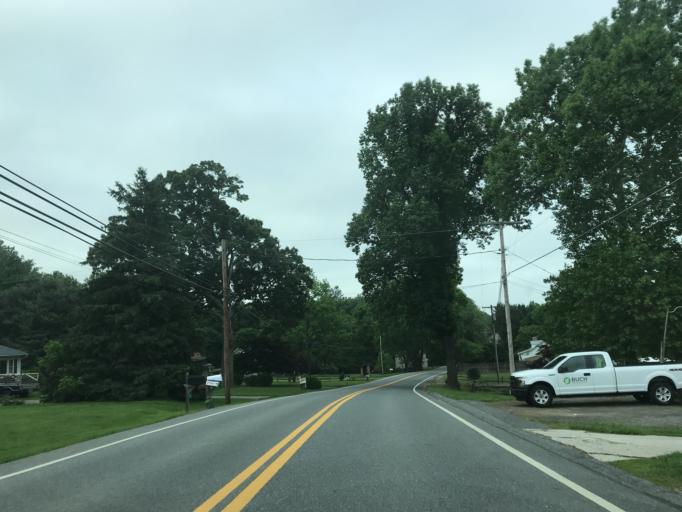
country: US
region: Maryland
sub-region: Frederick County
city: Thurmont
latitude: 39.5975
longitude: -77.4293
